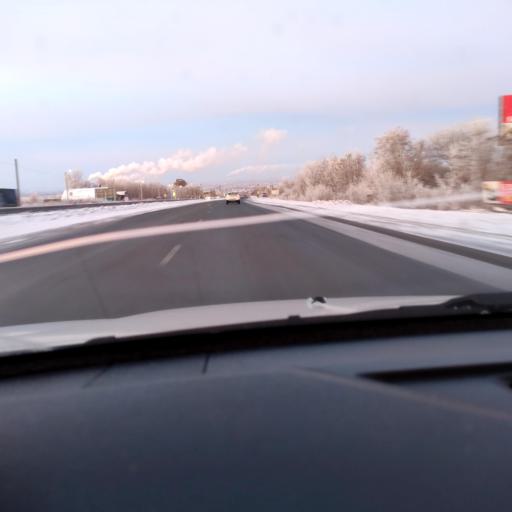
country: RU
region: Samara
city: Smyshlyayevka
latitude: 53.2593
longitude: 50.4498
